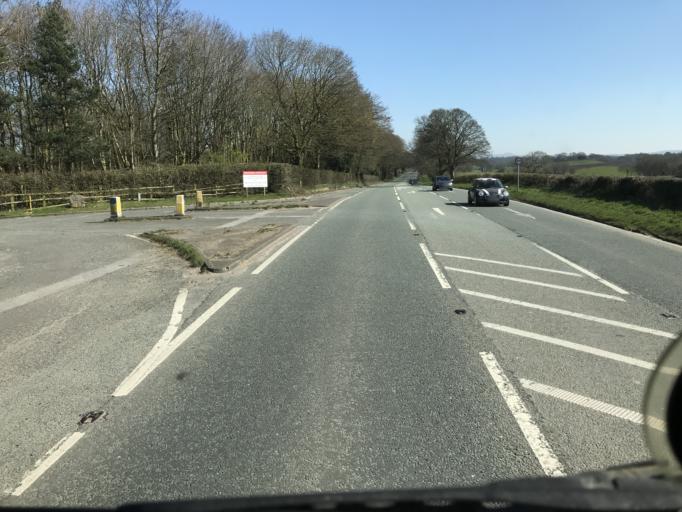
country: GB
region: England
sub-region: Cheshire East
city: Siddington
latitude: 53.2656
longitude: -2.2514
